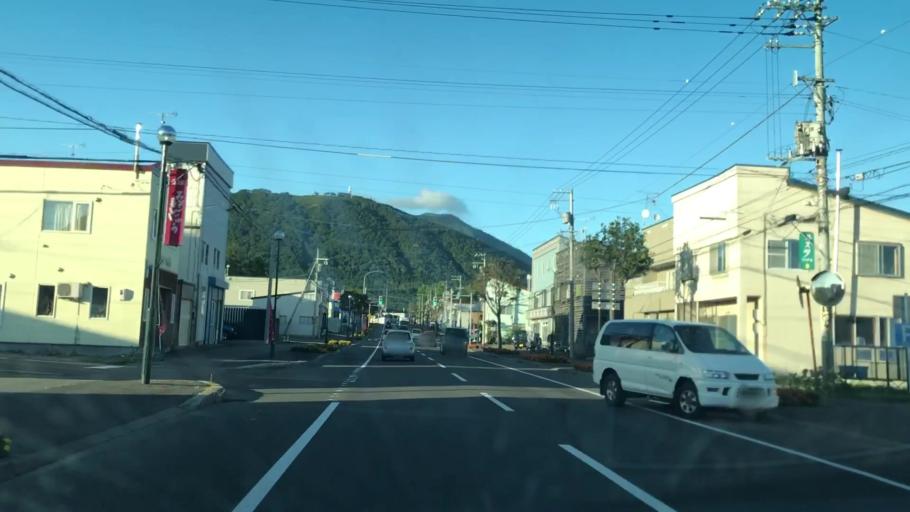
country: JP
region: Hokkaido
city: Niseko Town
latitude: 42.7348
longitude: 140.8744
